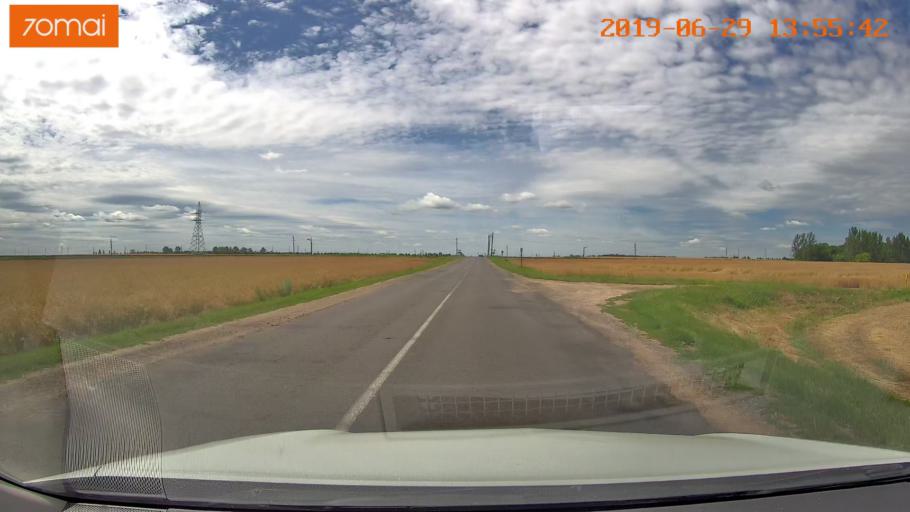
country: BY
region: Minsk
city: Slutsk
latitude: 52.9845
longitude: 27.5145
